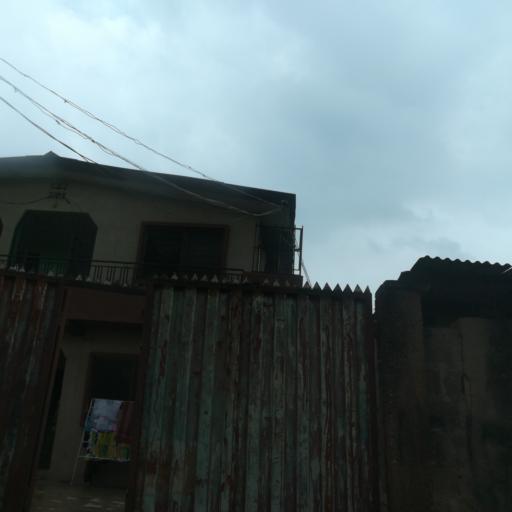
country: NG
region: Lagos
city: Agege
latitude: 6.5981
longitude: 3.2964
